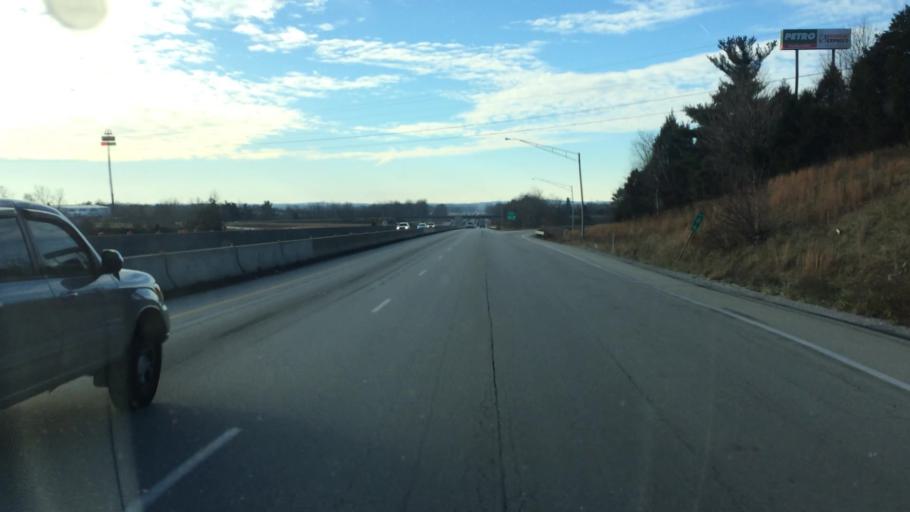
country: US
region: Kentucky
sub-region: Hardin County
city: Elizabethtown
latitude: 37.6011
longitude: -85.8678
